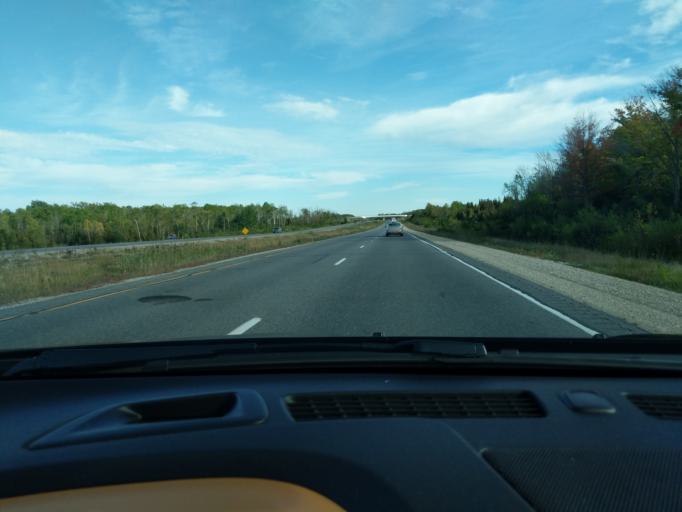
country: CA
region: Ontario
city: Collingwood
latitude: 44.4743
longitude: -80.1508
